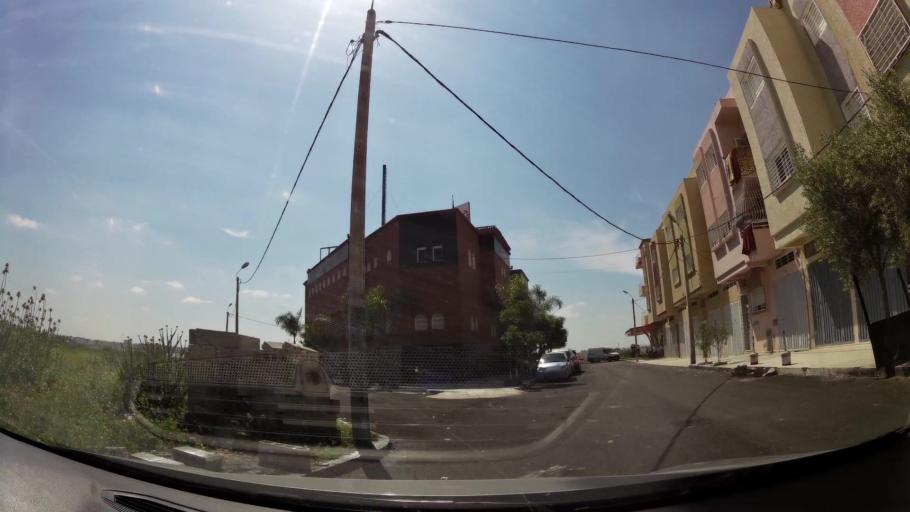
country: MA
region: Fes-Boulemane
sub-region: Fes
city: Fes
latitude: 34.0064
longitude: -5.0344
